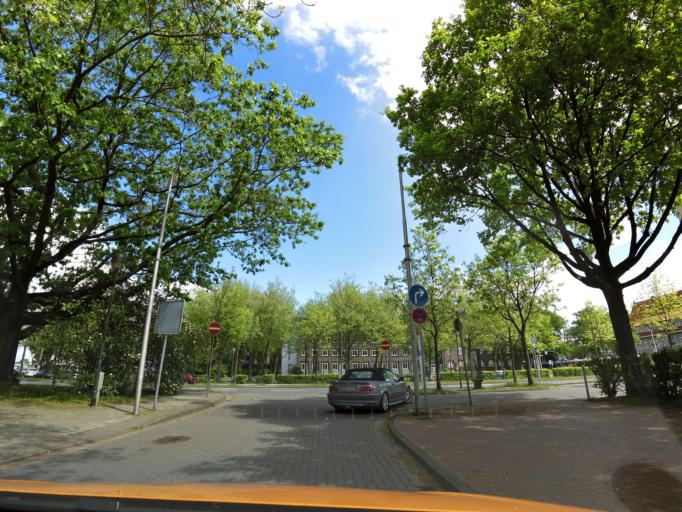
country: DE
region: Lower Saxony
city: Delmenhorst
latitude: 53.0478
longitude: 8.6258
